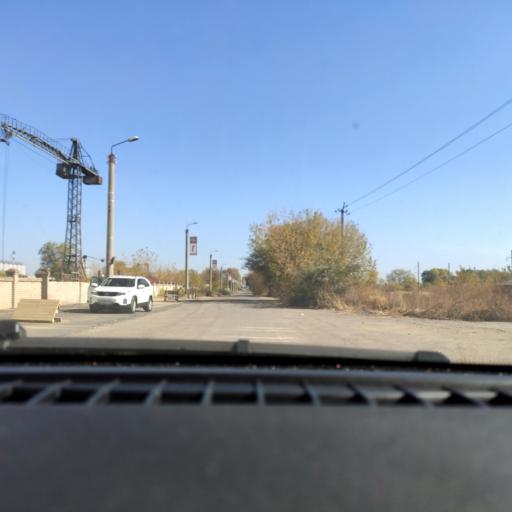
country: RU
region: Voronezj
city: Somovo
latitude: 51.6691
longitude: 39.2917
